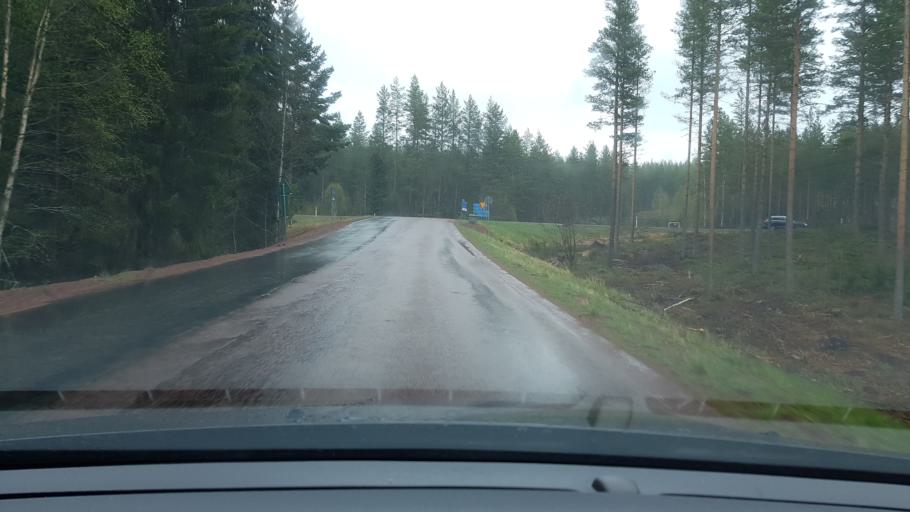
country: SE
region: Dalarna
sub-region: Alvdalens Kommun
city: AElvdalen
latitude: 61.1342
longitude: 14.1726
